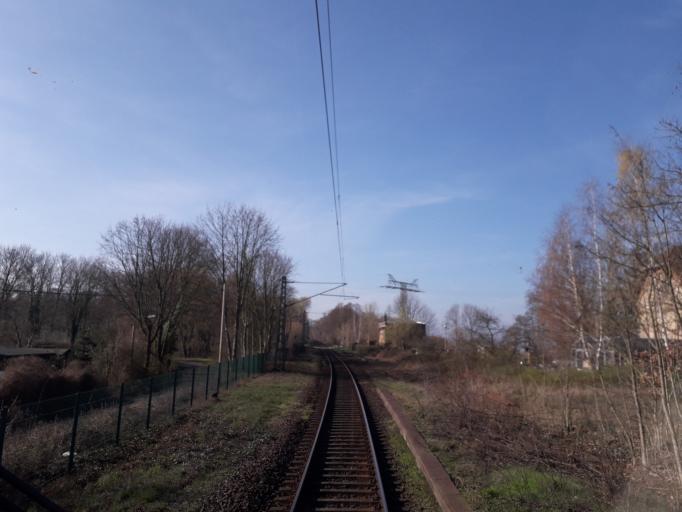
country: DE
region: Brandenburg
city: Werder
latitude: 52.3501
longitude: 12.9844
